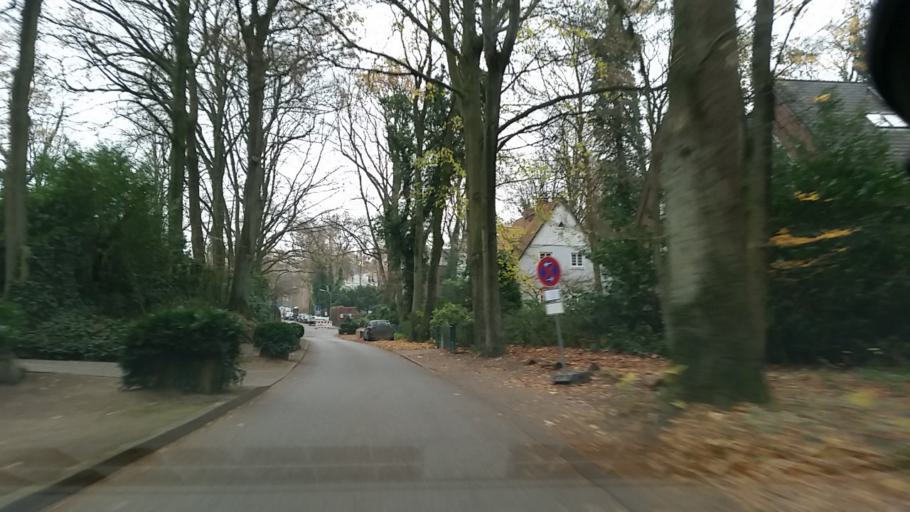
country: DE
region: Schleswig-Holstein
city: Rellingen
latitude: 53.5722
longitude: 9.7897
